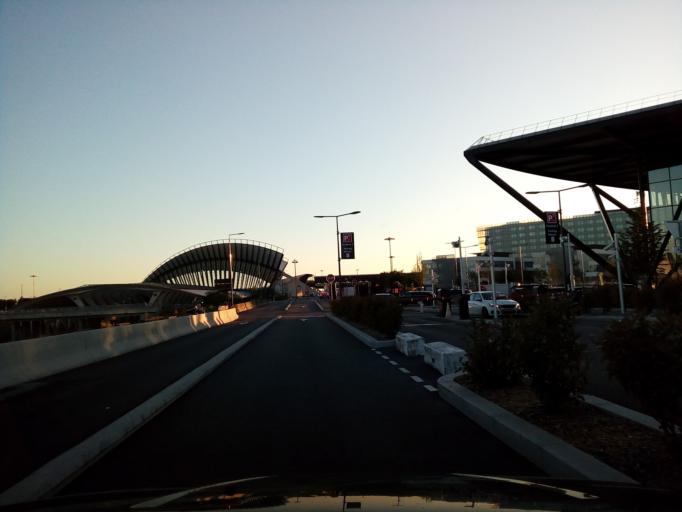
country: FR
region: Rhone-Alpes
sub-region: Departement du Rhone
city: Saint-Laurent-de-Mure
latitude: 45.7174
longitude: 5.0762
